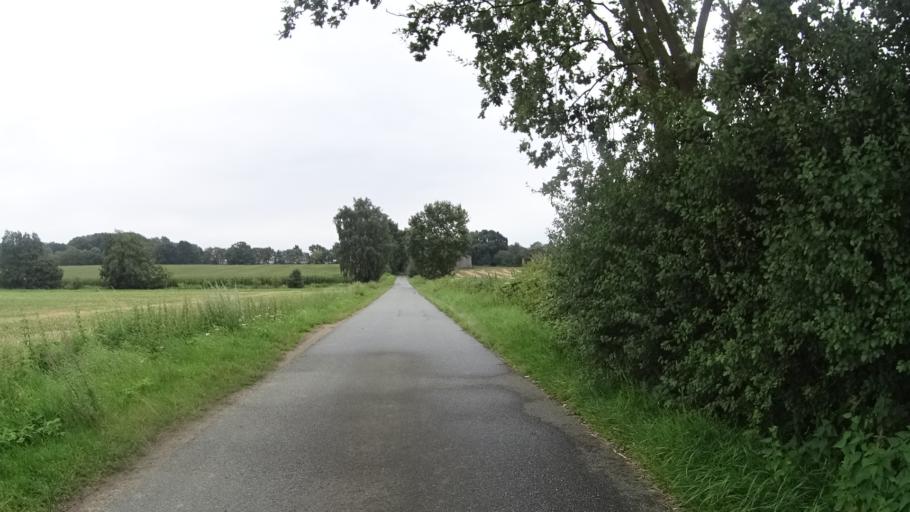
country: DE
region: Schleswig-Holstein
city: Lasbek
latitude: 53.7286
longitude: 10.3859
